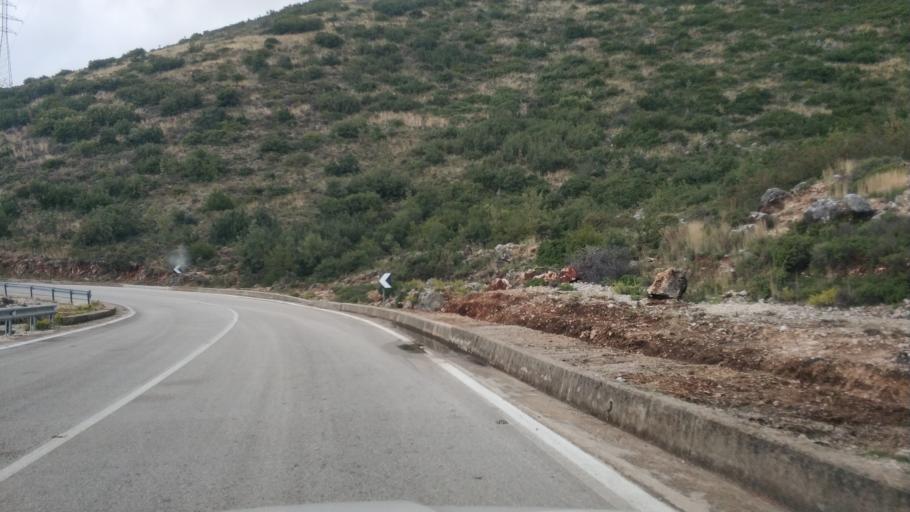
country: AL
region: Vlore
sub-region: Rrethi i Vlores
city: Vranisht
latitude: 40.1455
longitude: 19.6601
